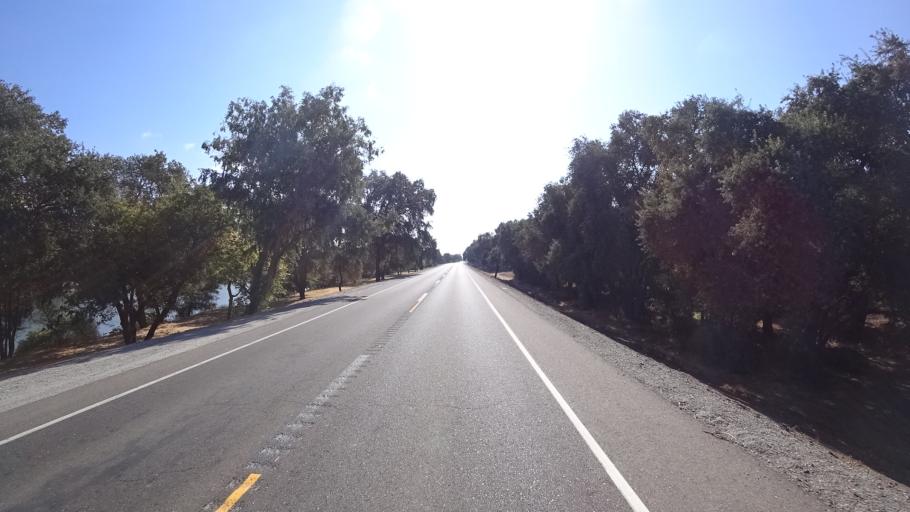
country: US
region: California
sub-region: Yolo County
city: West Sacramento
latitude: 38.6362
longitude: -121.5648
